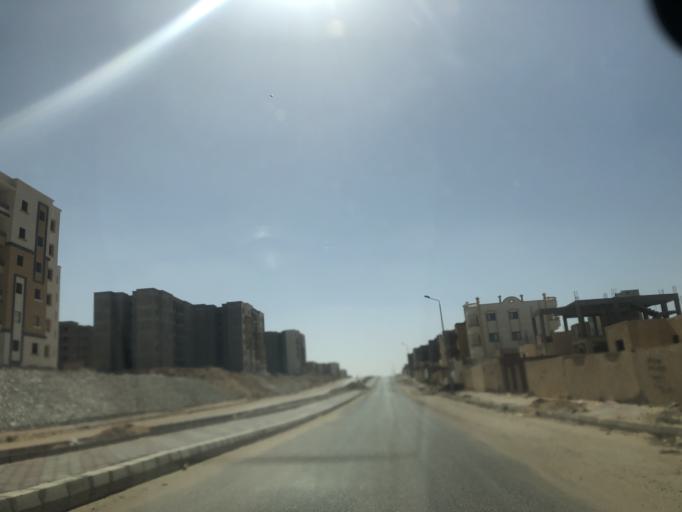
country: EG
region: Al Jizah
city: Madinat Sittah Uktubar
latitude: 29.9286
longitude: 31.0061
